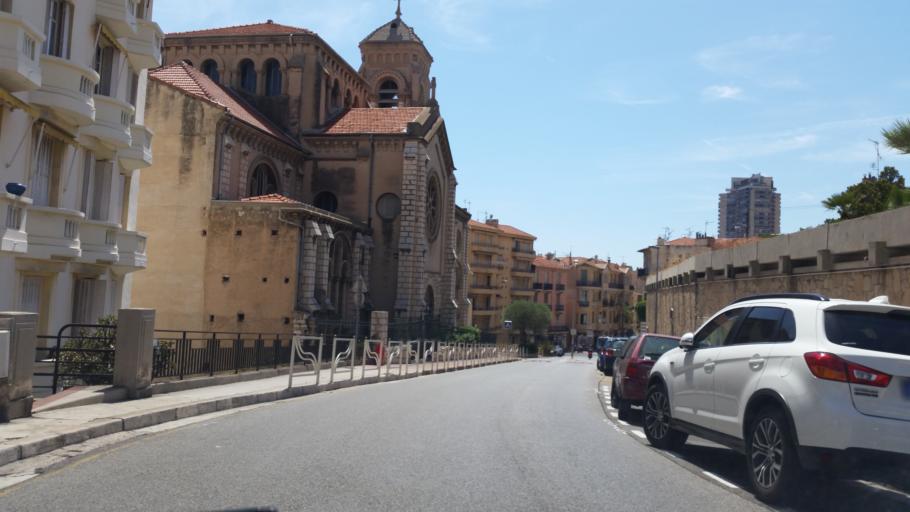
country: MC
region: Commune de Monaco
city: Monte-Carlo
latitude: 43.7455
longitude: 7.4275
